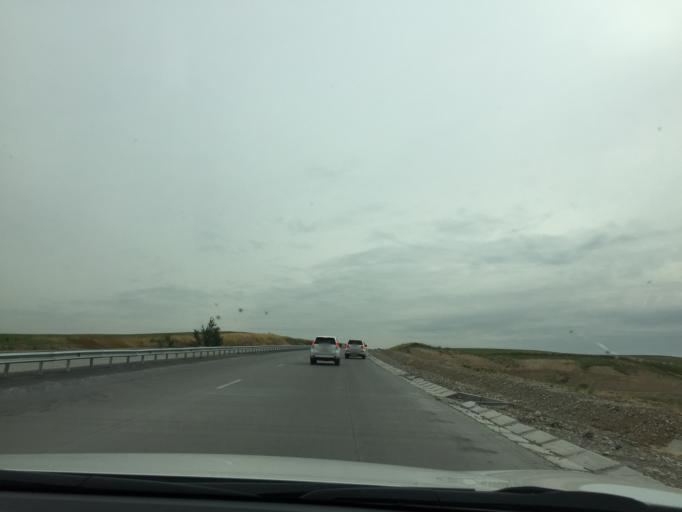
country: KZ
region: Ongtustik Qazaqstan
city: Aksu
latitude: 42.4442
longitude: 69.7302
